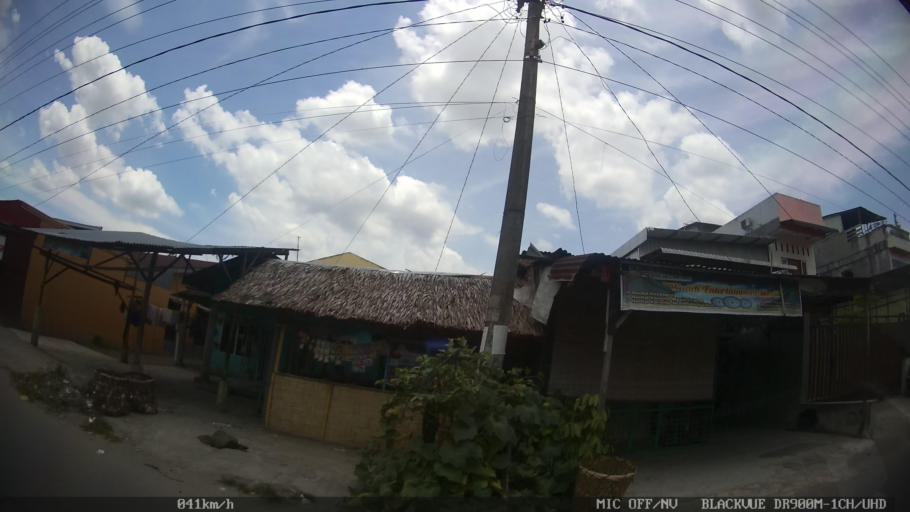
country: ID
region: North Sumatra
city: Binjai
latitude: 3.6179
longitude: 98.5183
